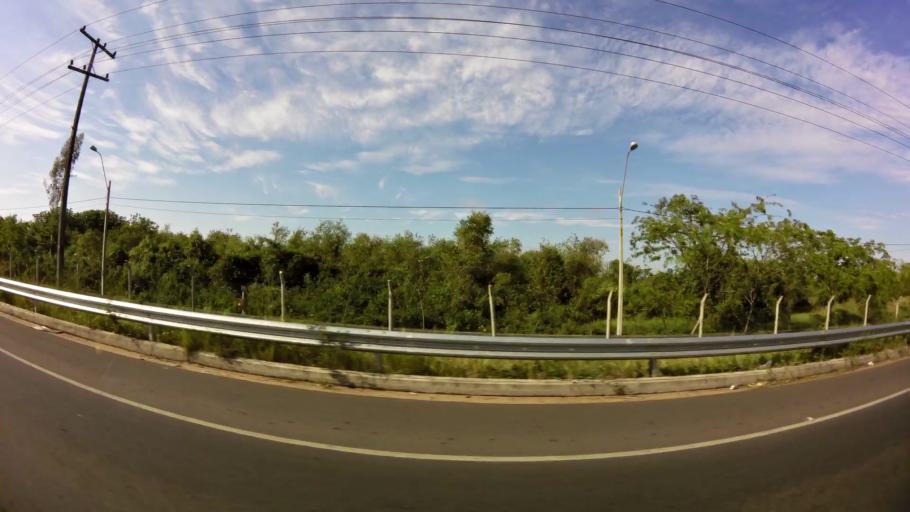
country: PY
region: Central
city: Fernando de la Mora
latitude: -25.2586
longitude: -57.5405
